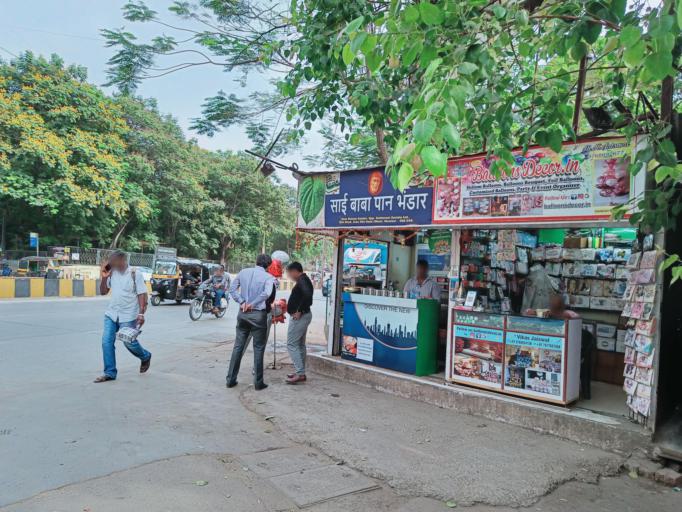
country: IN
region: Maharashtra
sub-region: Mumbai Suburban
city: Mumbai
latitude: 19.1130
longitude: 72.8299
